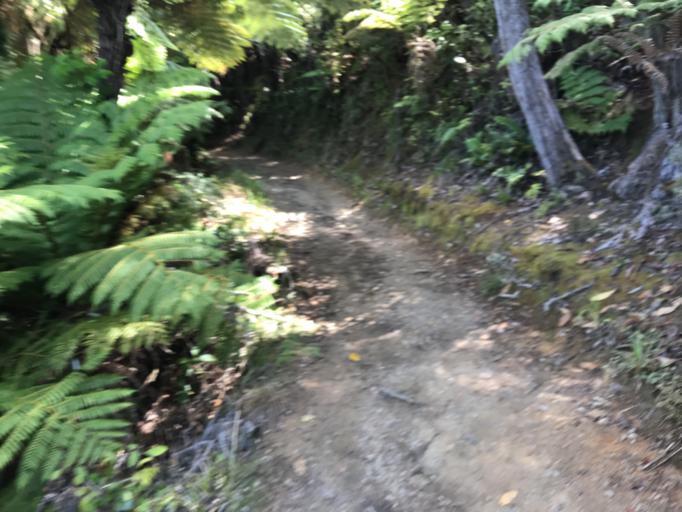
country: NZ
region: Marlborough
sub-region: Marlborough District
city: Picton
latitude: -41.2574
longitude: 173.9376
